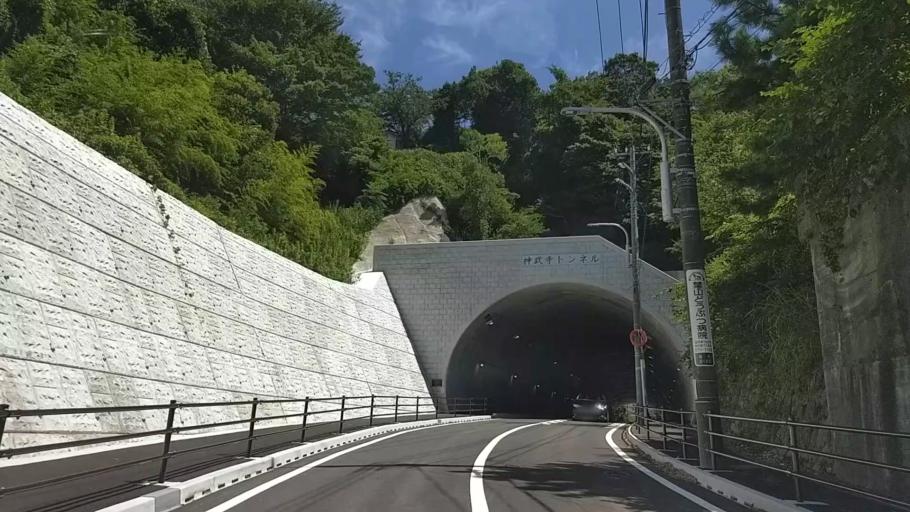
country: JP
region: Kanagawa
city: Zushi
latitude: 35.3036
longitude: 139.5993
